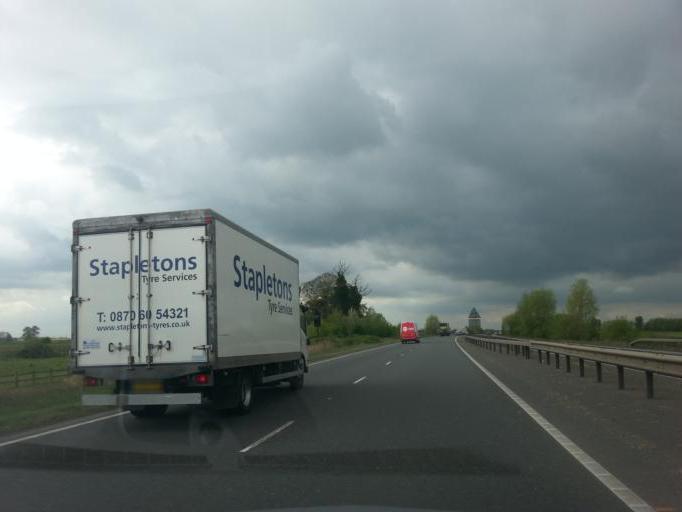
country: GB
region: England
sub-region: Peterborough
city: Thorney
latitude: 52.6217
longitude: -0.0636
